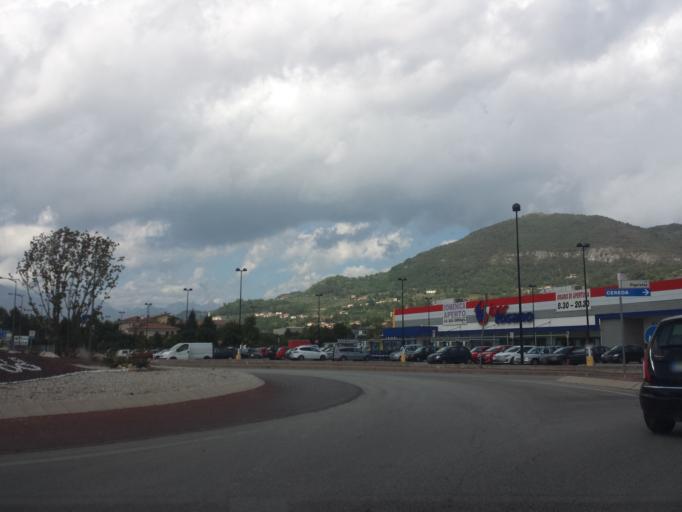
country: IT
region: Veneto
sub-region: Provincia di Vicenza
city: Cereda-Cozza Cornedo
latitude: 45.5988
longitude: 11.3659
